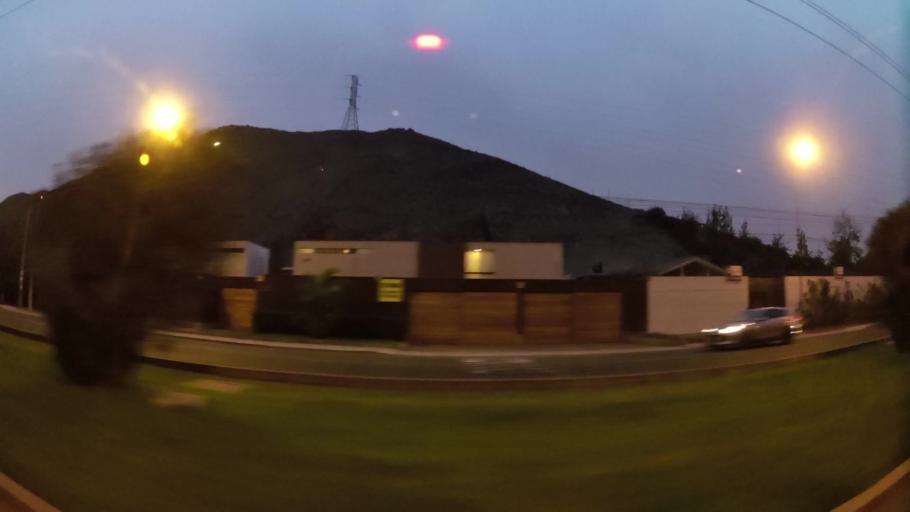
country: PE
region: Lima
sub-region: Lima
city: La Molina
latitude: -12.0808
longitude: -76.9555
